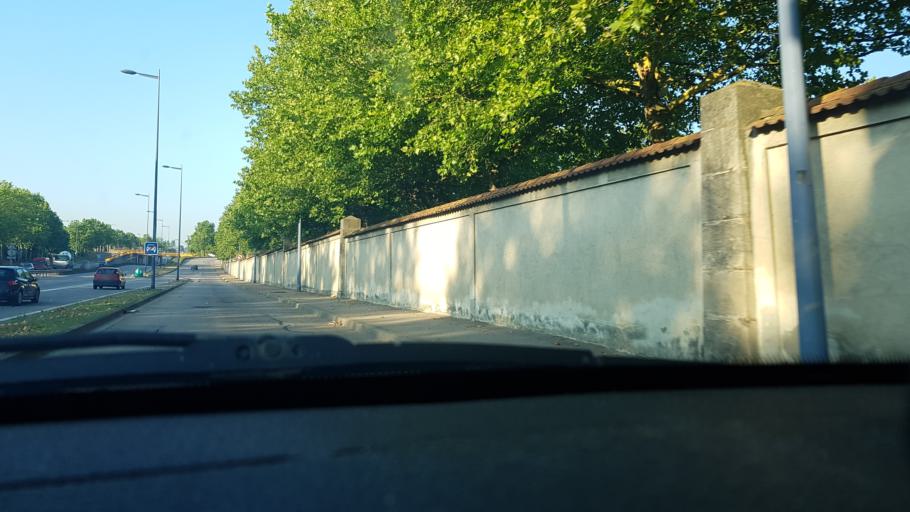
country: FR
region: Lorraine
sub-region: Departement de Meurthe-et-Moselle
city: Jarville-la-Malgrange
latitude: 48.6709
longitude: 6.1928
